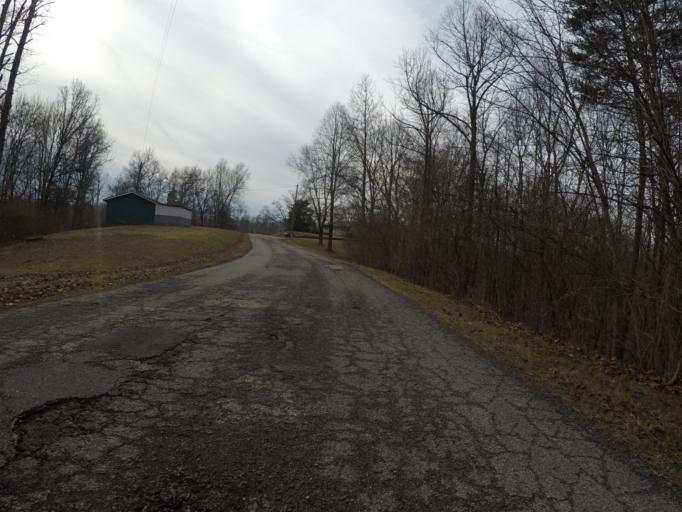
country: US
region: West Virginia
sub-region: Wayne County
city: Lavalette
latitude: 38.3574
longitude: -82.4111
